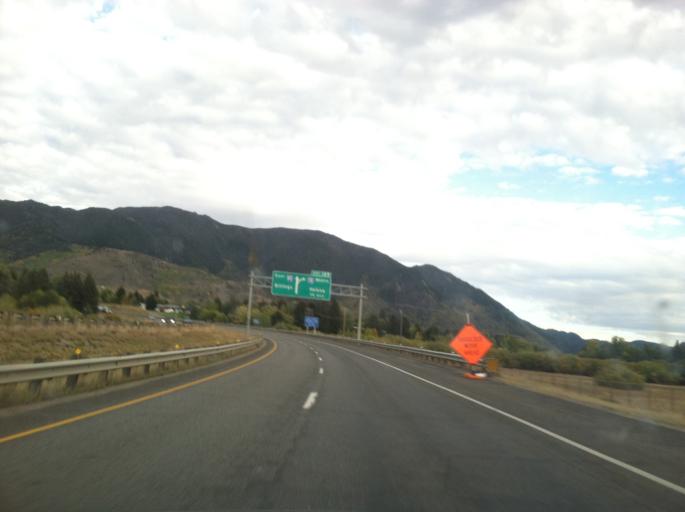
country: US
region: Montana
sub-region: Silver Bow County
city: Butte
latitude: 45.9808
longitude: -112.5036
